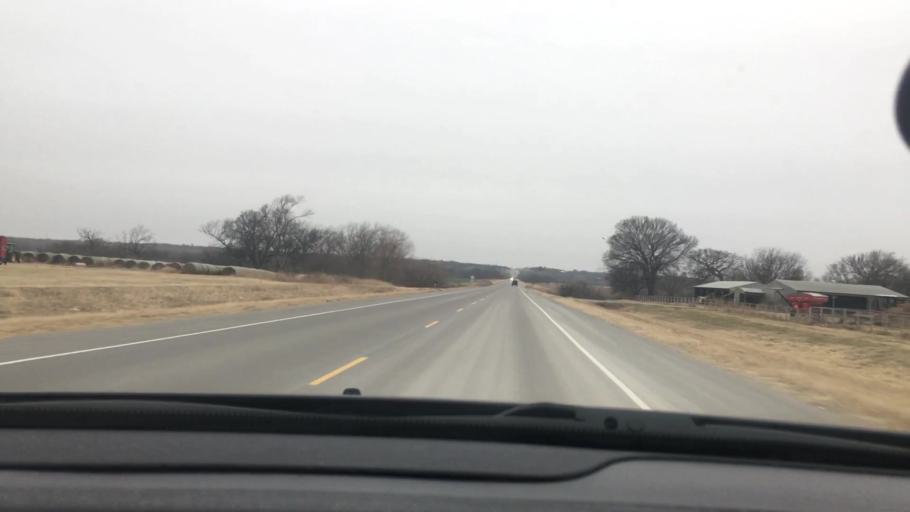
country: US
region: Oklahoma
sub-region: Garvin County
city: Wynnewood
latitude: 34.6226
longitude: -97.1784
